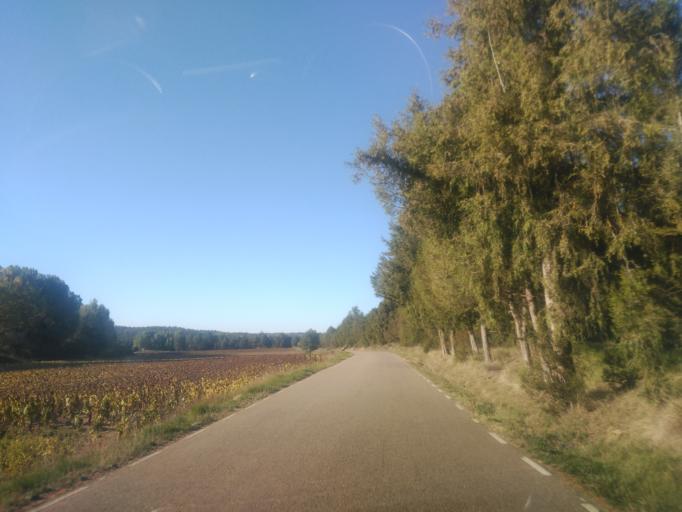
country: ES
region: Castille and Leon
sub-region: Provincia de Burgos
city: Brazacorta
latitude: 41.7053
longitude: -3.3914
